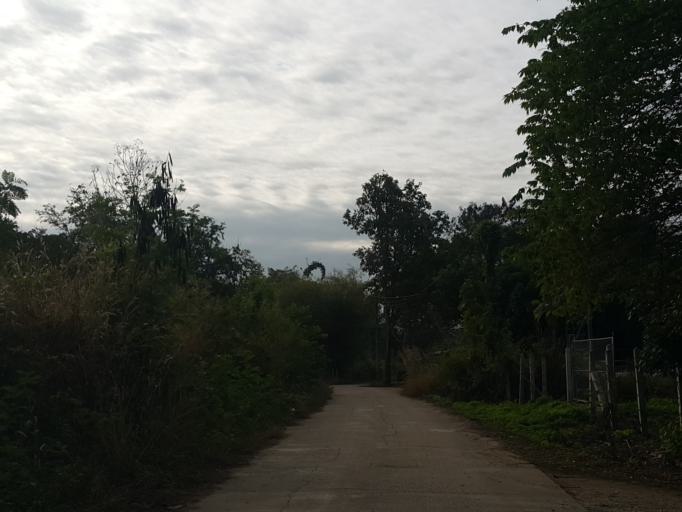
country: TH
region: Lampang
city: Mae Mo
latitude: 18.2494
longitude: 99.5977
